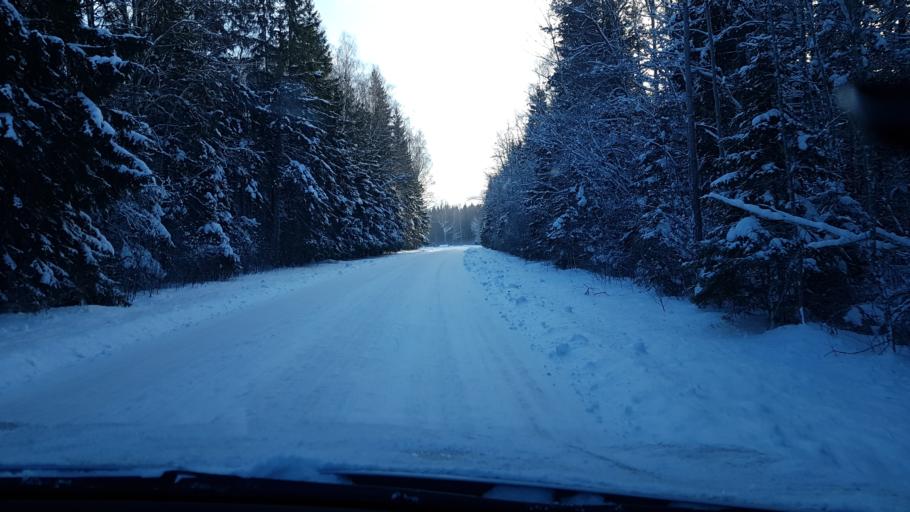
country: EE
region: Harju
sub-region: Nissi vald
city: Turba
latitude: 59.1308
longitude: 24.1962
